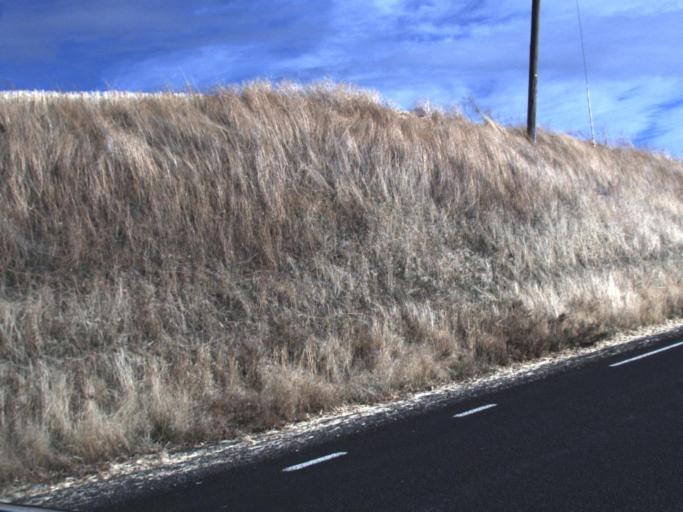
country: US
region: Washington
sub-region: Whitman County
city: Colfax
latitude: 46.9379
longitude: -117.1847
